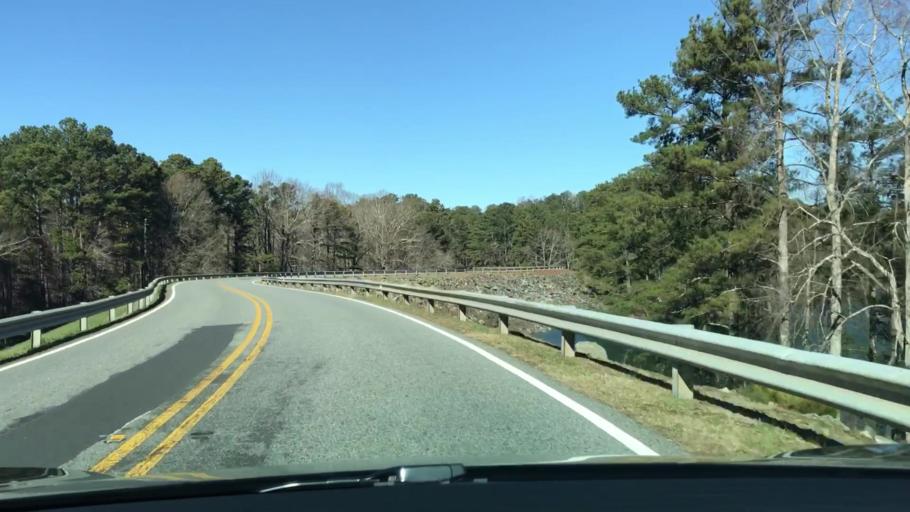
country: US
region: Georgia
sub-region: Forsyth County
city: Cumming
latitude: 34.1709
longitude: -84.0779
